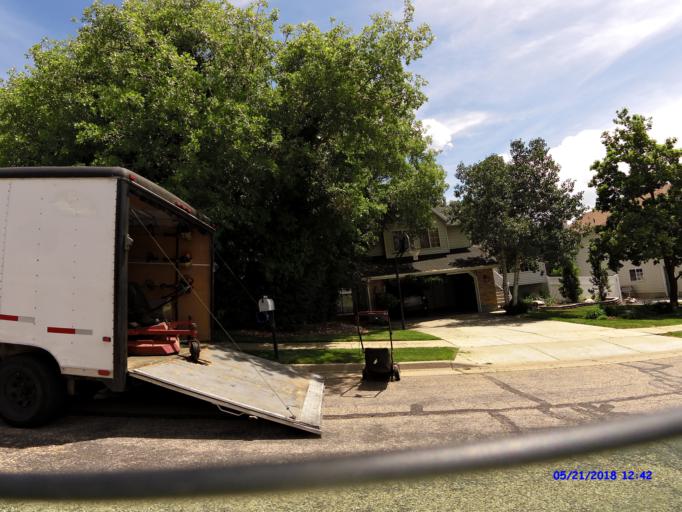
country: US
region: Utah
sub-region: Weber County
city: Washington Terrace
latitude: 41.1705
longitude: -111.9497
